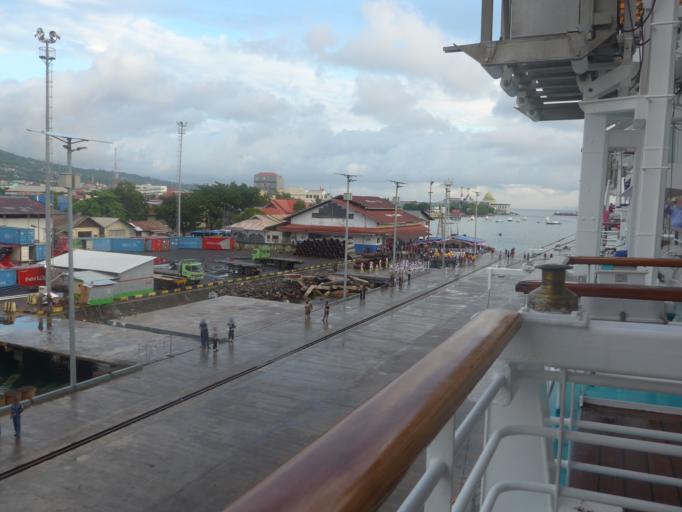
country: ID
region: Maluku Utara
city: Ternate
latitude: 0.7799
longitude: 127.3884
